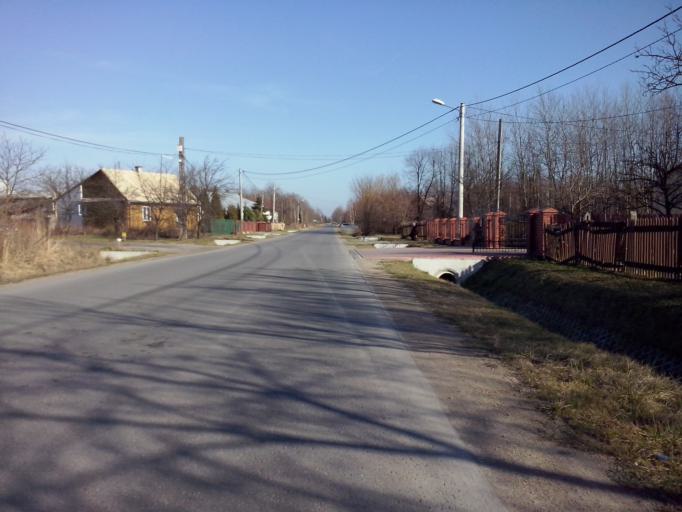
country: PL
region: Subcarpathian Voivodeship
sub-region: Powiat nizanski
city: Krzeszow
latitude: 50.4152
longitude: 22.3627
